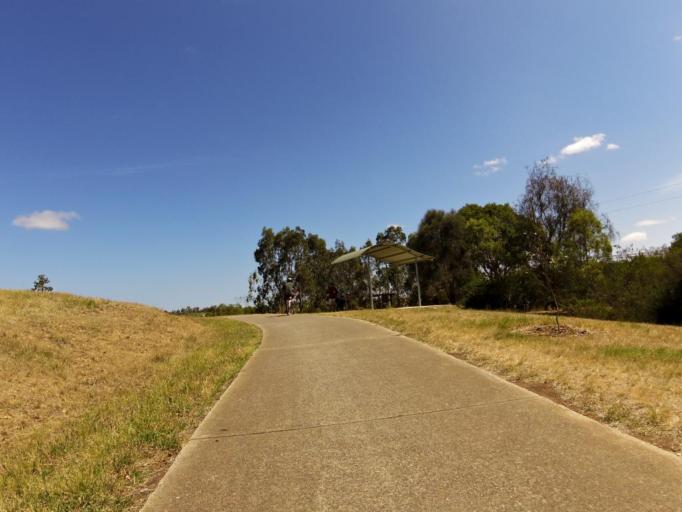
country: AU
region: Victoria
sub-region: Hume
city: Meadow Heights
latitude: -37.6587
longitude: 144.9083
